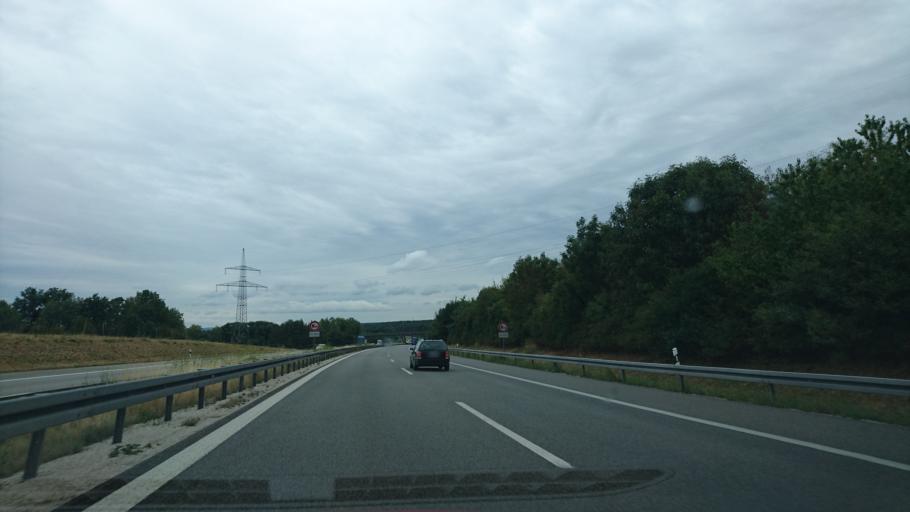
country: DE
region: Bavaria
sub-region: Upper Palatinate
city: Maxhutte-Haidhof
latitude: 49.2067
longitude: 12.1170
